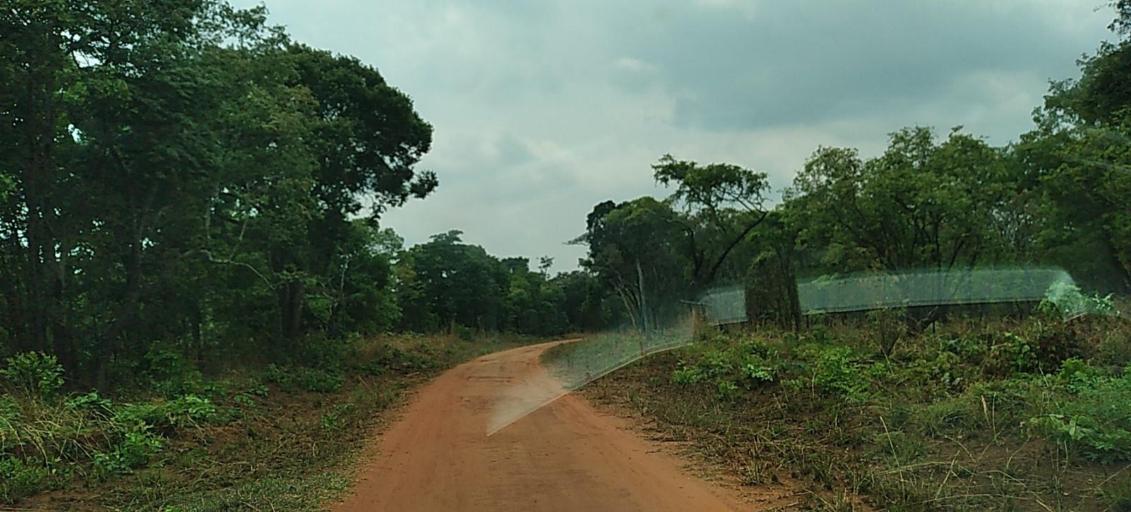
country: ZM
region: North-Western
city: Mwinilunga
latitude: -11.5529
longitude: 24.7734
